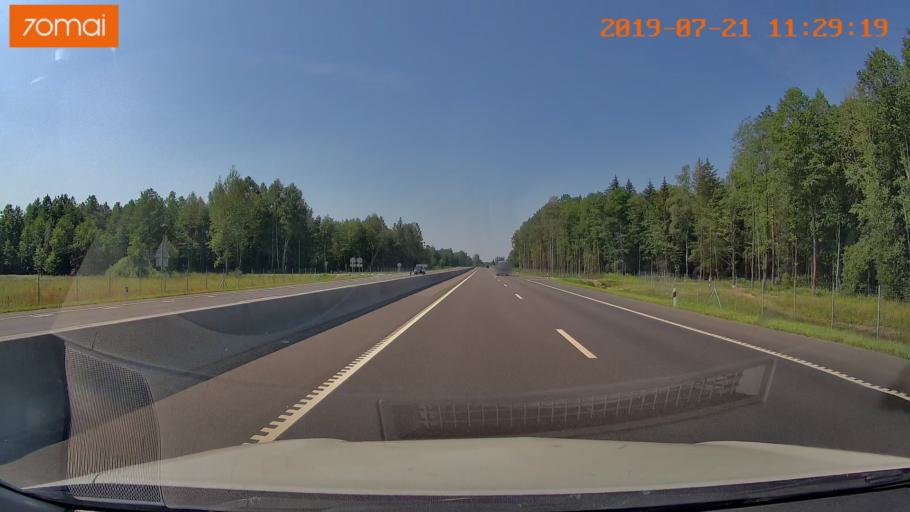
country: BY
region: Minsk
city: Valozhyn
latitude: 54.0287
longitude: 26.4418
